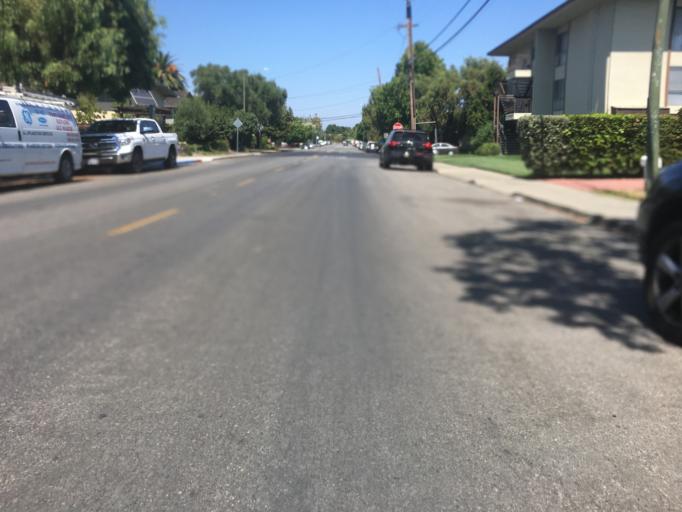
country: US
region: California
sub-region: Santa Clara County
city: Los Altos
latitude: 37.4068
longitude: -122.1137
